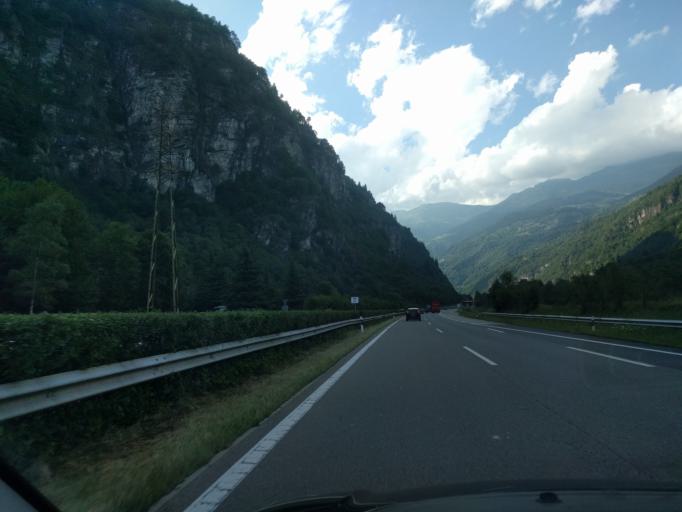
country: CH
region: Ticino
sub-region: Leventina District
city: Faido
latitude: 46.4447
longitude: 8.8323
